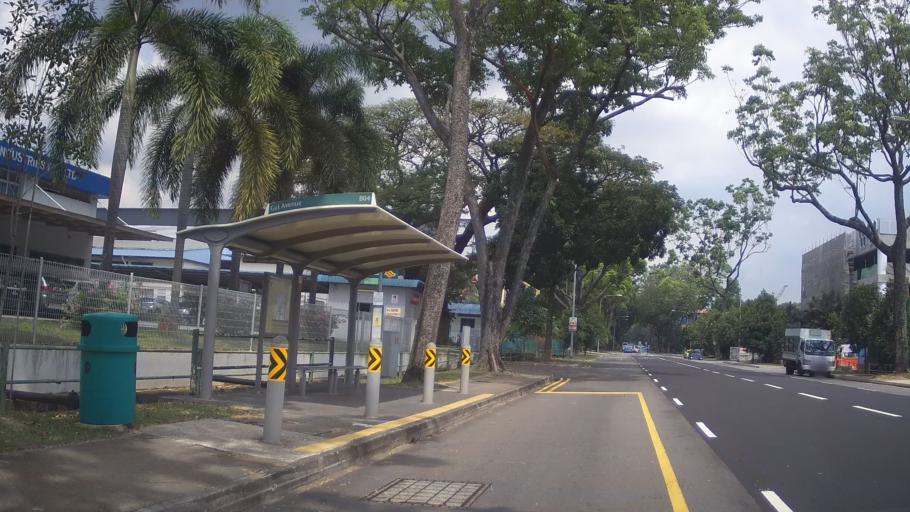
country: MY
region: Johor
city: Johor Bahru
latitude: 1.3146
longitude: 103.6687
